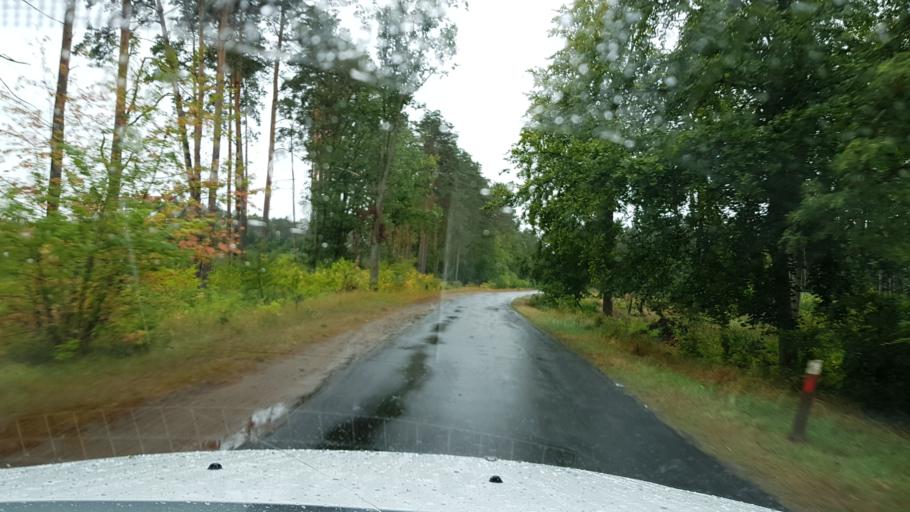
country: DE
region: Brandenburg
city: Schoneberg
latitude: 52.9651
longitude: 14.2038
